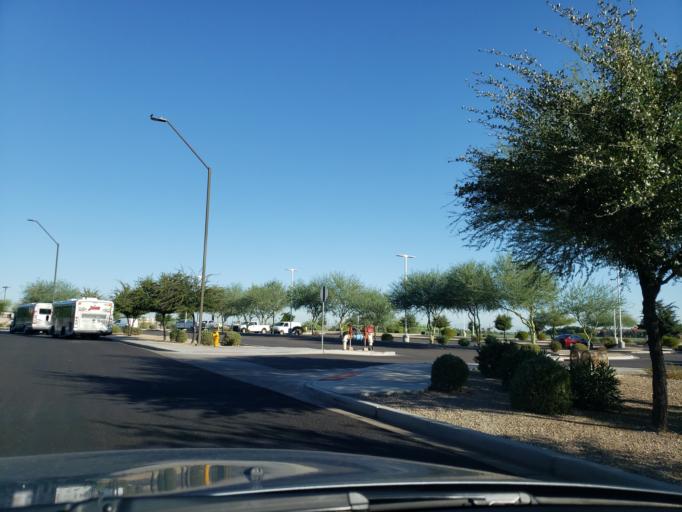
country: US
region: Arizona
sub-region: Maricopa County
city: Tolleson
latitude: 33.4447
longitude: -112.3035
